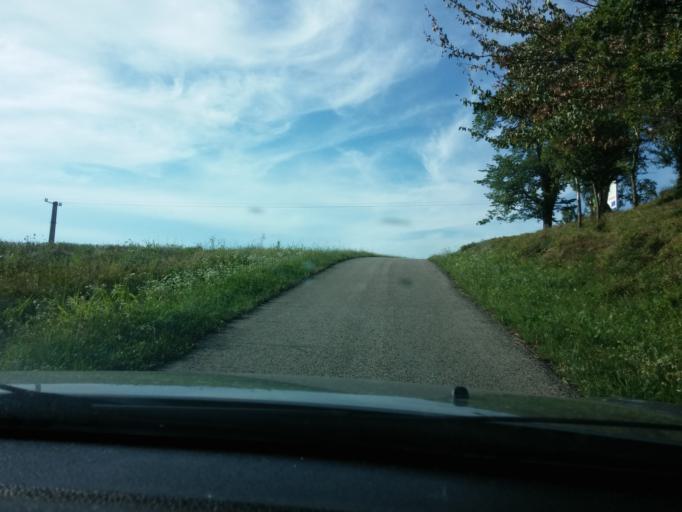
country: HU
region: Somogy
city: Kaposmero
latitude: 46.2765
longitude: 17.7401
